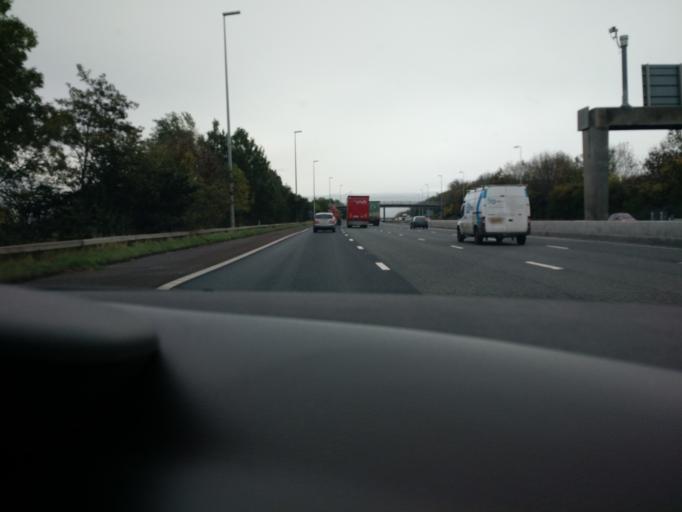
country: GB
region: England
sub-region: Lancashire
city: Goosnargh
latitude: 53.7989
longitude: -2.6858
